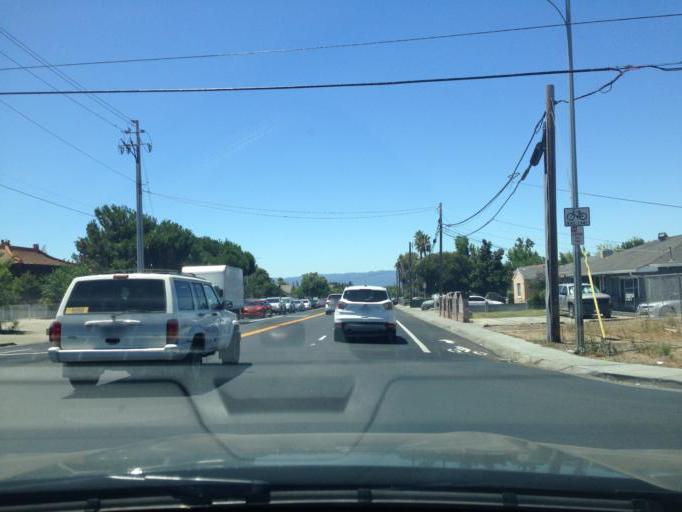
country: US
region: California
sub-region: Santa Clara County
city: Alum Rock
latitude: 37.3739
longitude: -121.8376
